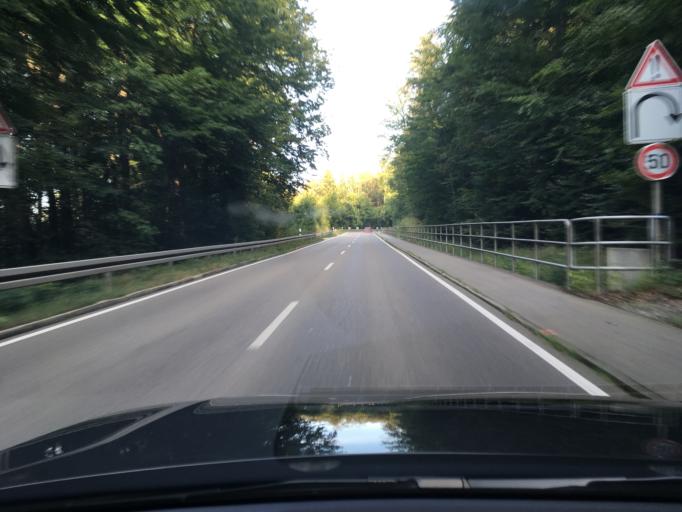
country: DE
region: Baden-Wuerttemberg
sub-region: Regierungsbezirk Stuttgart
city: Urbach
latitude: 48.7931
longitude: 9.5612
